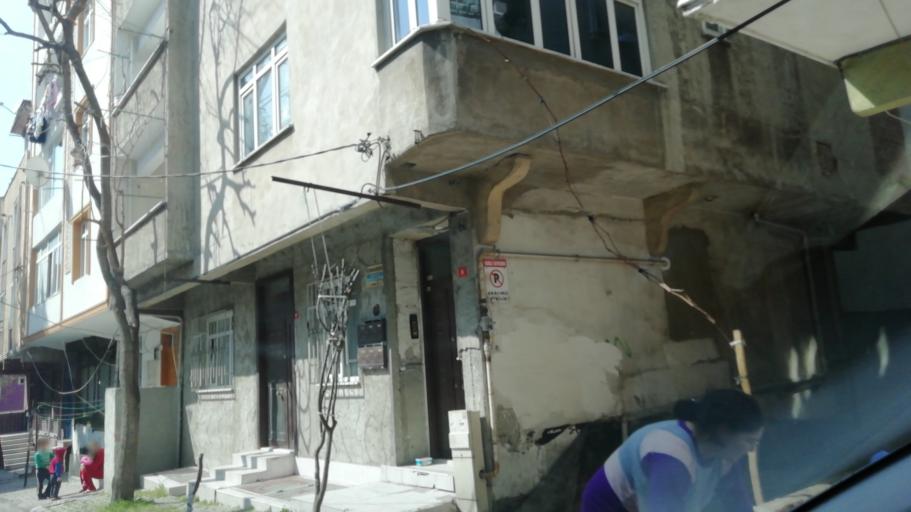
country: TR
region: Istanbul
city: Mahmutbey
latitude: 41.0374
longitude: 28.8217
